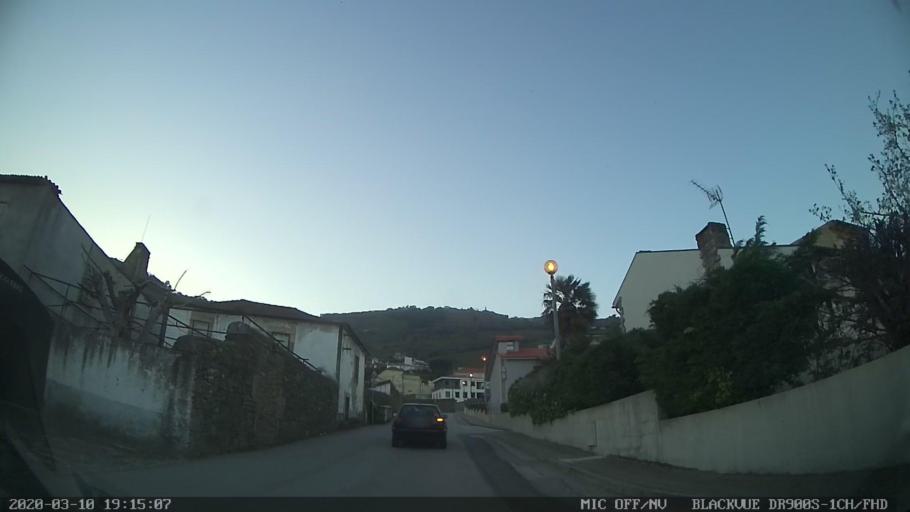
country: PT
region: Vila Real
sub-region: Peso da Regua
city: Godim
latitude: 41.1681
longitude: -7.8062
